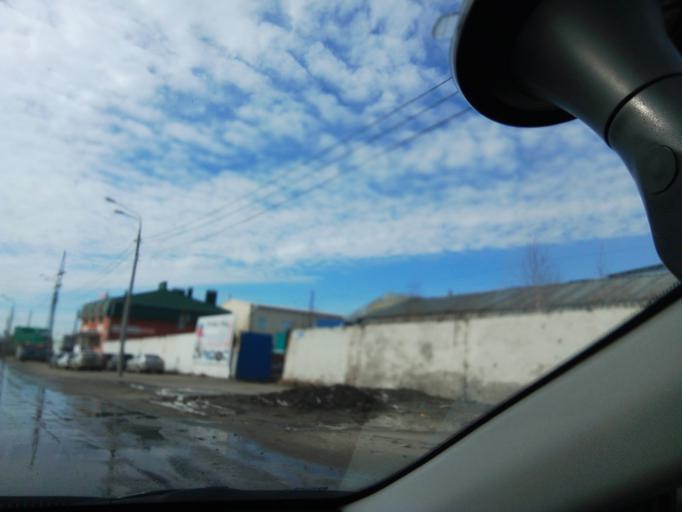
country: RU
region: Chuvashia
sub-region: Cheboksarskiy Rayon
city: Cheboksary
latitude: 56.1065
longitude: 47.2475
